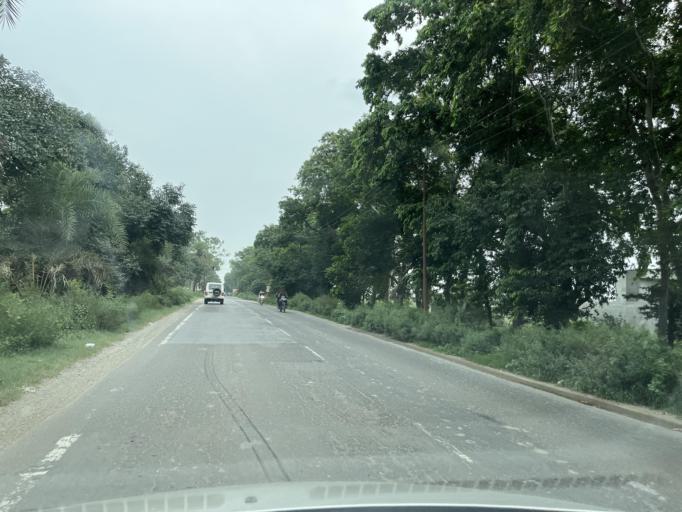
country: IN
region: Uttar Pradesh
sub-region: Rampur
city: Bilaspur
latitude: 29.0297
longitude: 79.2643
